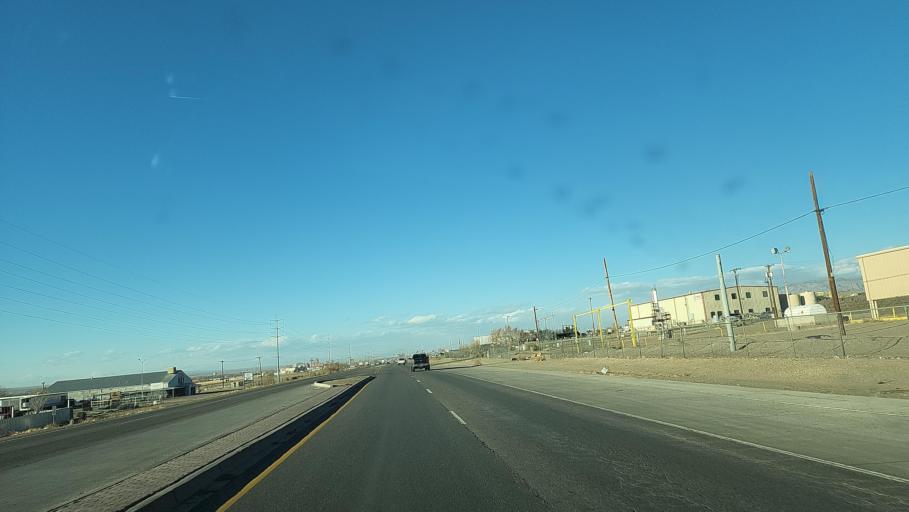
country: US
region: New Mexico
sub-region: Bernalillo County
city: South Valley
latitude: 35.0202
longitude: -106.6470
